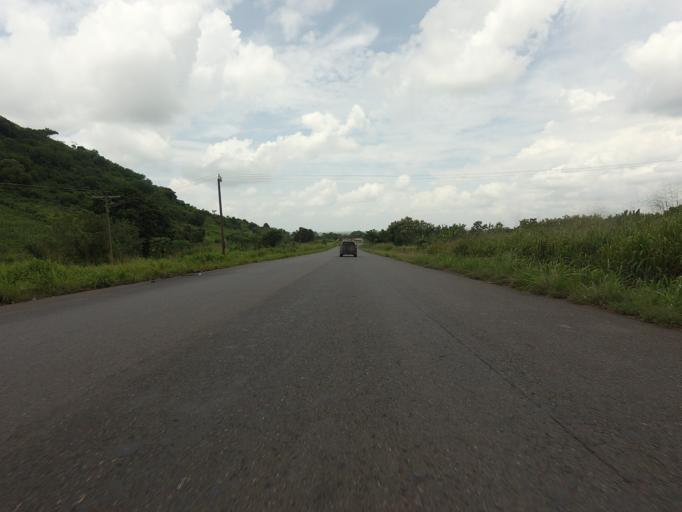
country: GH
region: Volta
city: Ho
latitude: 6.4234
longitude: 0.1706
